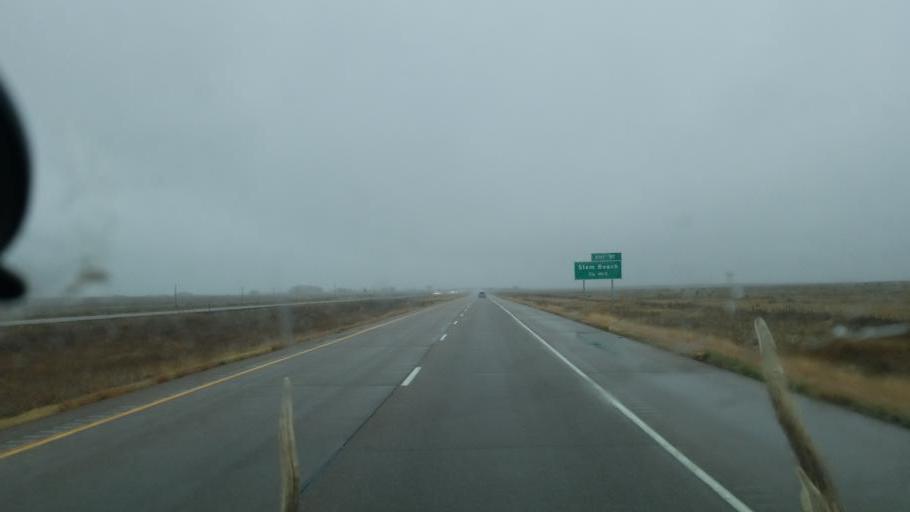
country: US
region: Colorado
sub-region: Pueblo County
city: Pueblo
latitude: 38.1494
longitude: -104.6539
